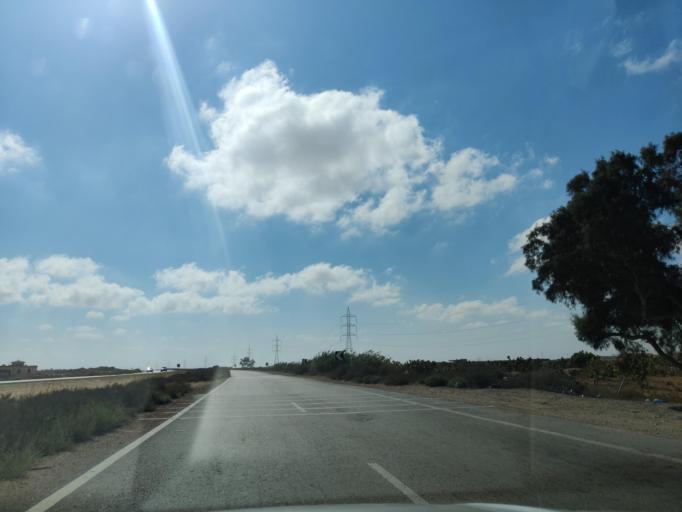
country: EG
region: Muhafazat Matruh
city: Al `Alamayn
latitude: 31.0546
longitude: 28.2609
